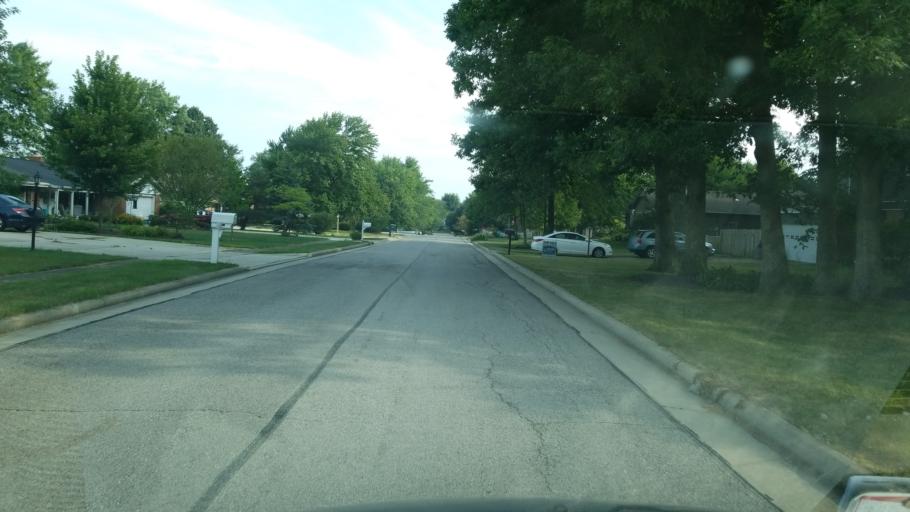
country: US
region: Ohio
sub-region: Crawford County
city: Bucyrus
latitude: 40.7916
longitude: -82.9558
